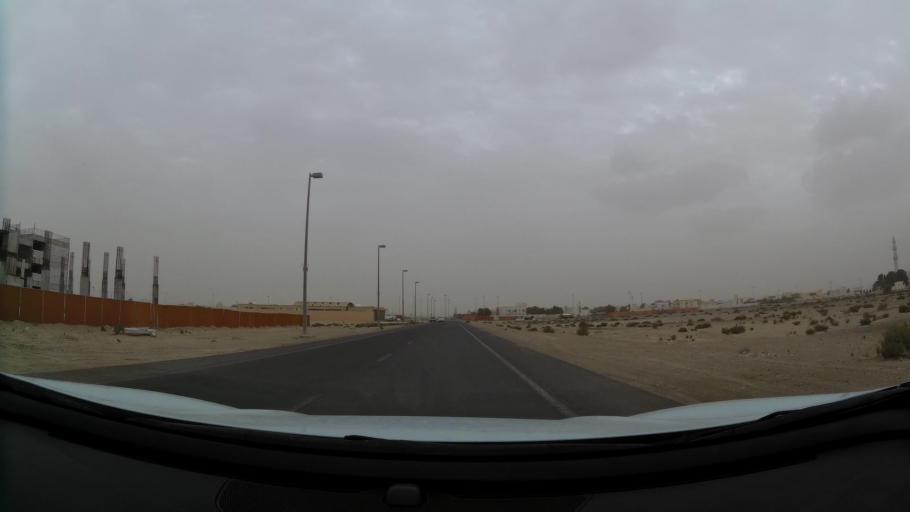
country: AE
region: Abu Dhabi
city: Abu Dhabi
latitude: 24.4232
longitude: 54.7285
